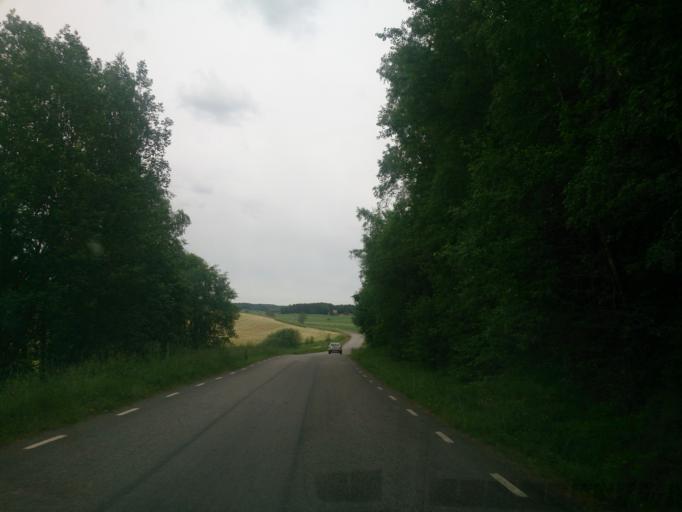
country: SE
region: OEstergoetland
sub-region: Valdemarsviks Kommun
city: Gusum
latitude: 58.3293
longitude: 16.4241
